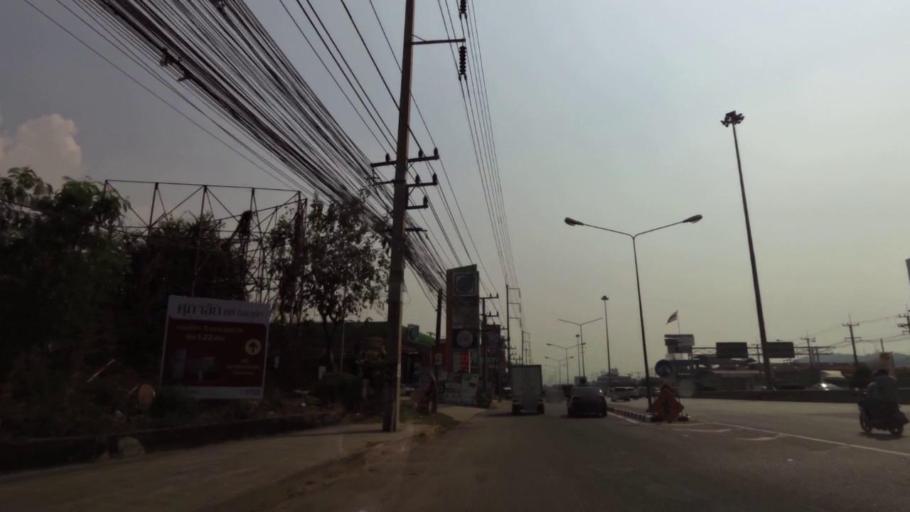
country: TH
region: Chon Buri
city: Chon Buri
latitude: 13.4138
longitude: 100.9993
